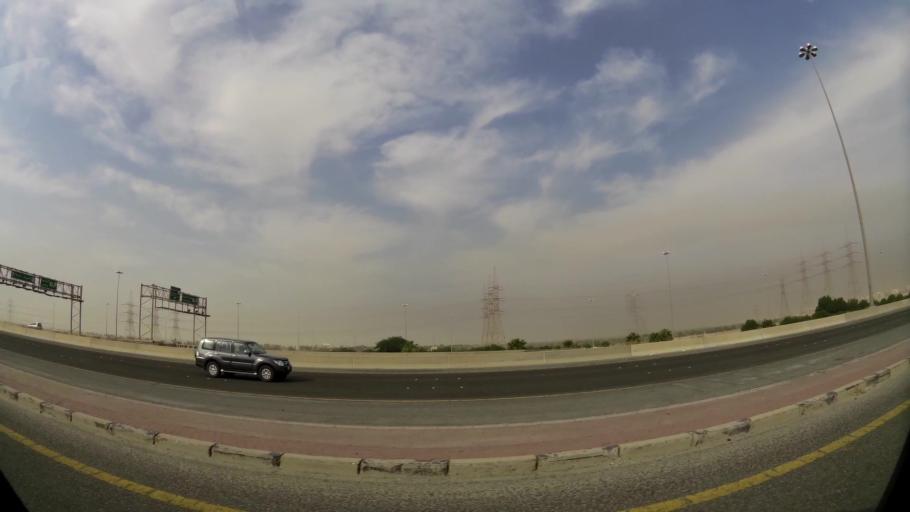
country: KW
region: Muhafazat al Jahra'
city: Al Jahra'
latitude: 29.3129
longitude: 47.7853
